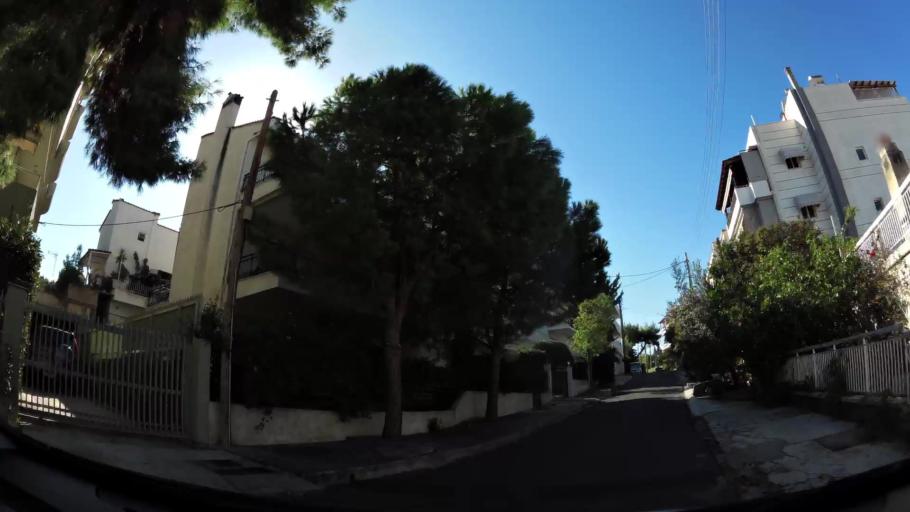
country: GR
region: Attica
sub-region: Nomarchia Athinas
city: Glyfada
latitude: 37.8572
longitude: 23.7687
